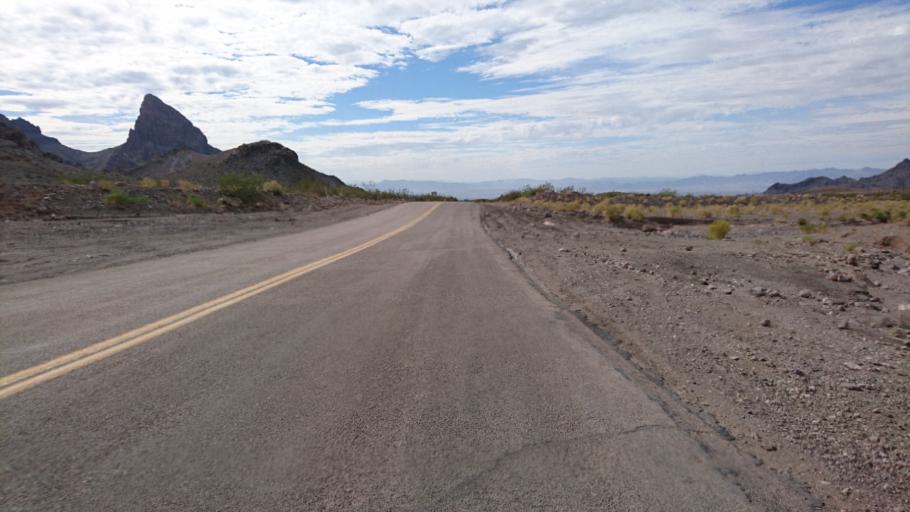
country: US
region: Arizona
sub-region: Mohave County
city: Mohave Valley
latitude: 35.0040
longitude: -114.3999
